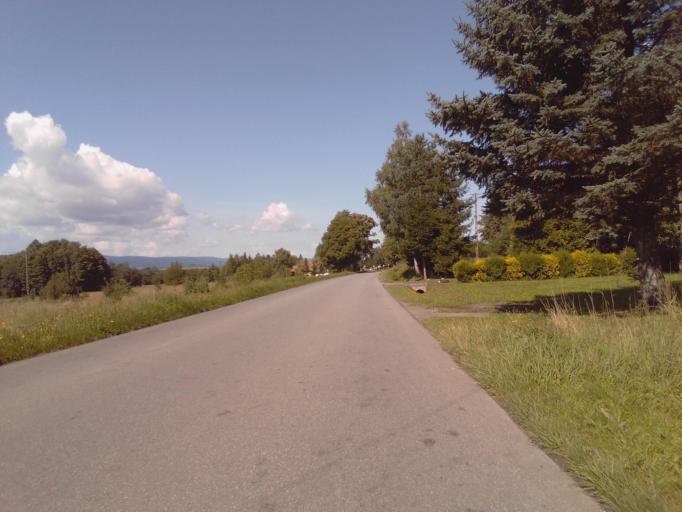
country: PL
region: Subcarpathian Voivodeship
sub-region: Powiat jasielski
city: Nowy Zmigrod
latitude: 49.6134
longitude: 21.5937
